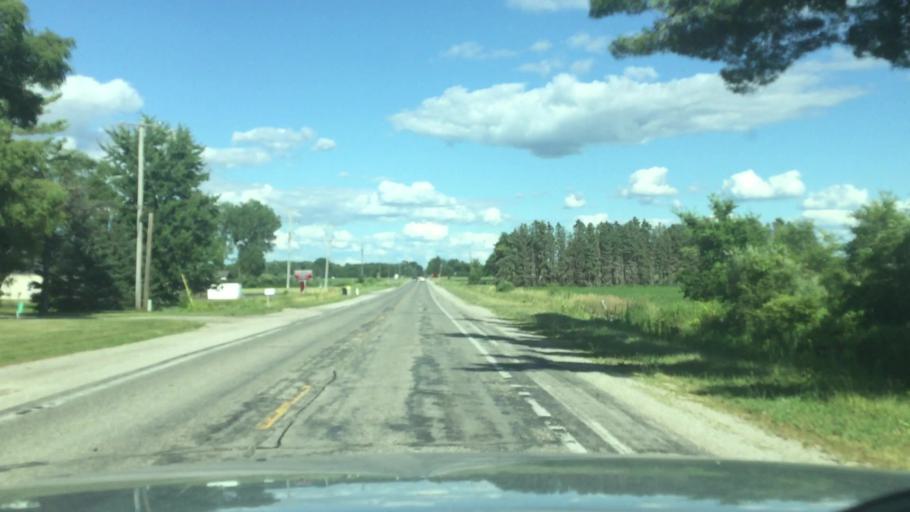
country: US
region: Michigan
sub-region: Saginaw County
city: Shields
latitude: 43.3798
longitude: -84.1193
